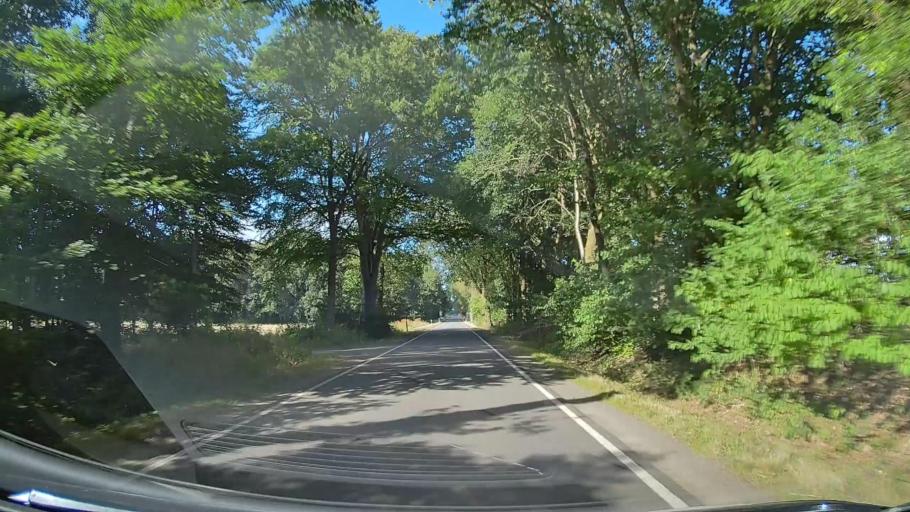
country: DE
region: Lower Saxony
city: Loningen
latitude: 52.7659
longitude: 7.7813
